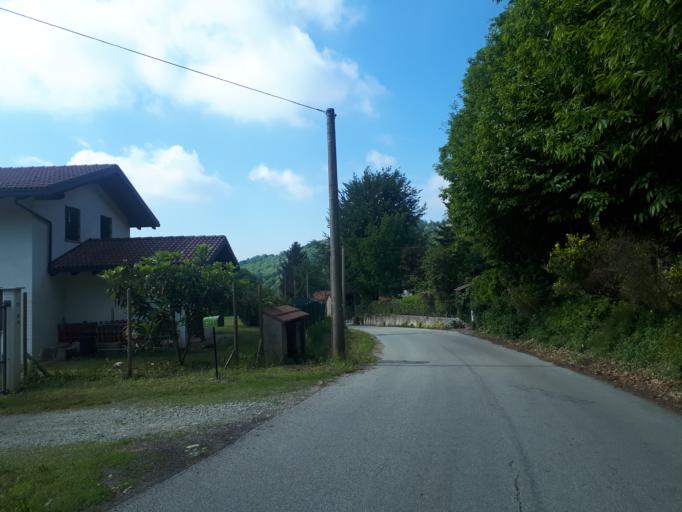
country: IT
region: Piedmont
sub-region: Provincia di Torino
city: Vialfre
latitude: 45.3784
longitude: 7.8233
